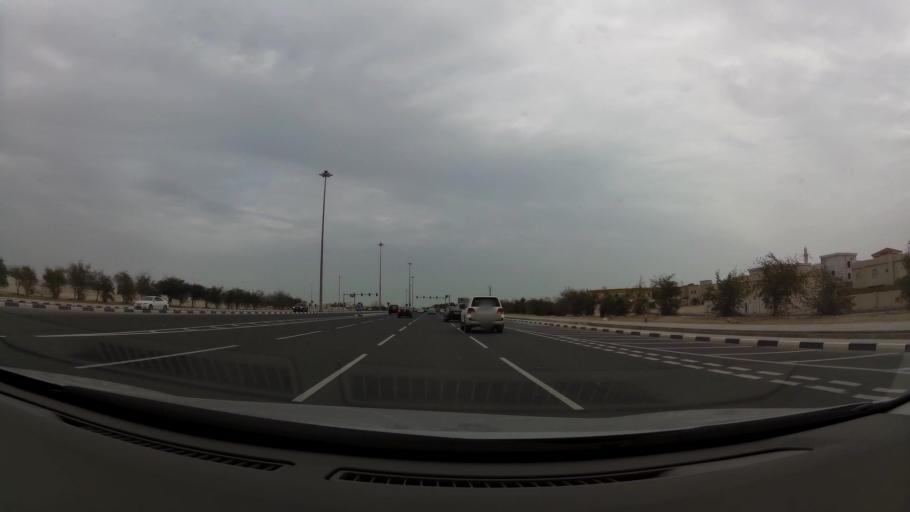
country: QA
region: Baladiyat ad Dawhah
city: Doha
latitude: 25.3485
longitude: 51.4863
